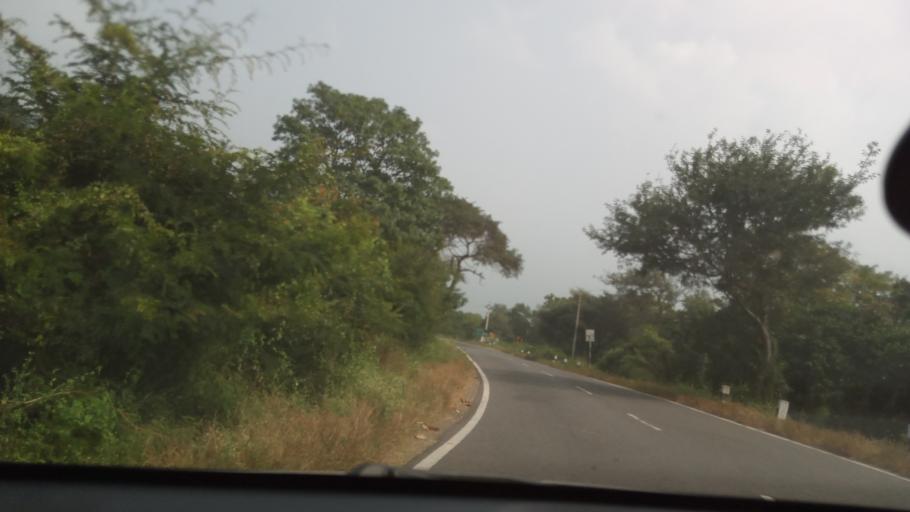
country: IN
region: Tamil Nadu
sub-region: Erode
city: Sathyamangalam
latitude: 11.5830
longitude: 77.1329
